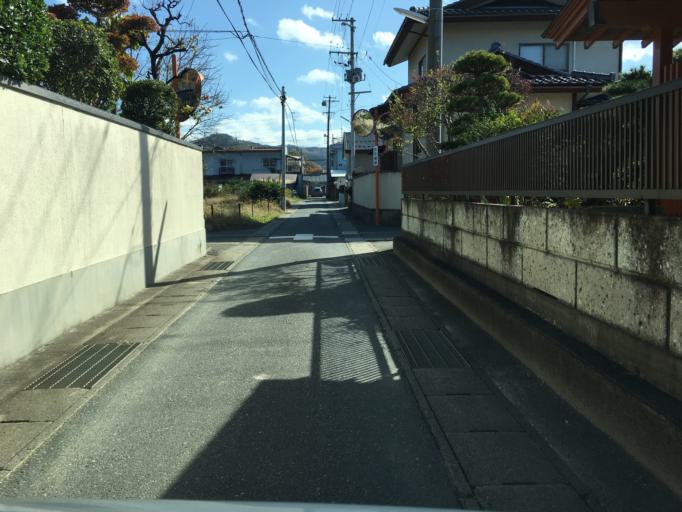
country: JP
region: Fukushima
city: Fukushima-shi
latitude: 37.7853
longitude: 140.5029
